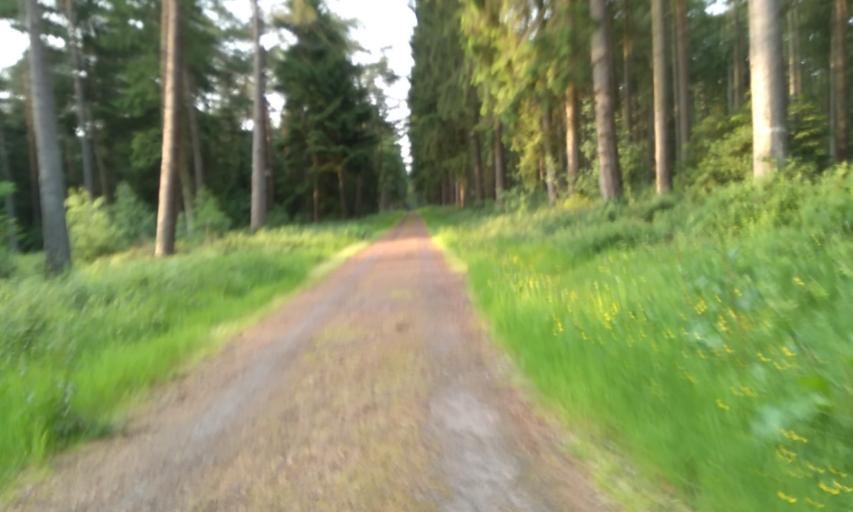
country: DE
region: Lower Saxony
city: Agathenburg
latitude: 53.5269
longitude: 9.5086
